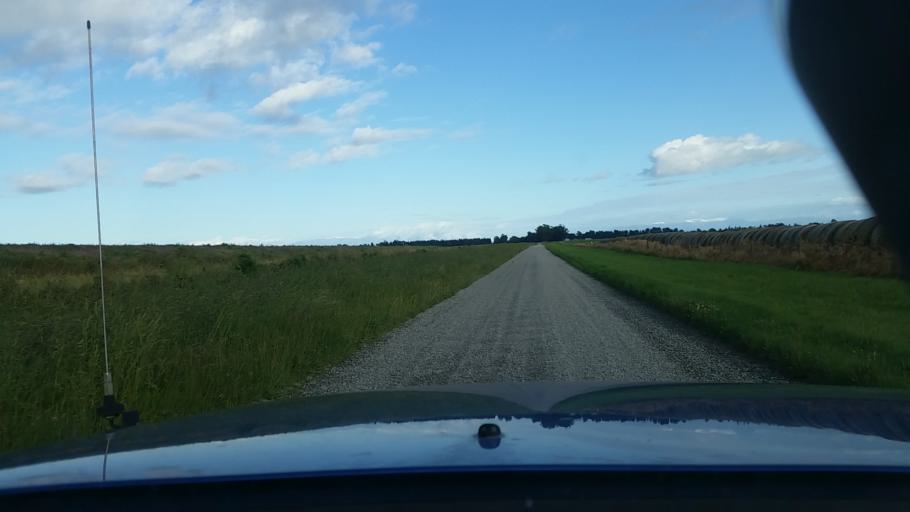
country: NZ
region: Canterbury
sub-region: Ashburton District
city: Rakaia
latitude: -43.7774
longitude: 172.0425
